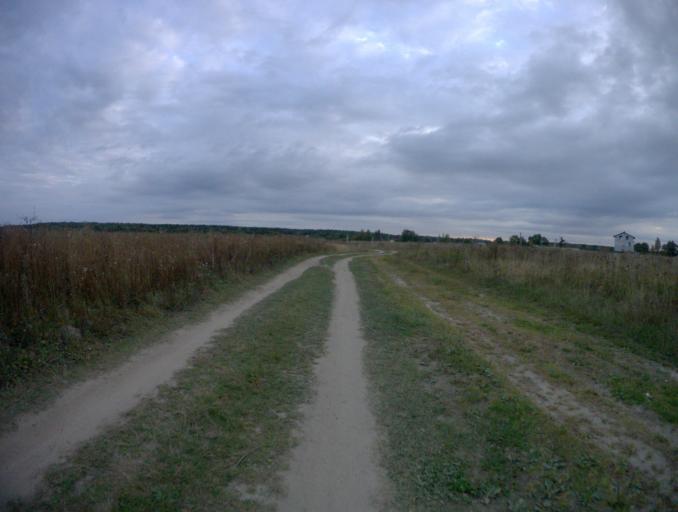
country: RU
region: Vladimir
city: Bogolyubovo
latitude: 56.1165
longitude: 40.5347
